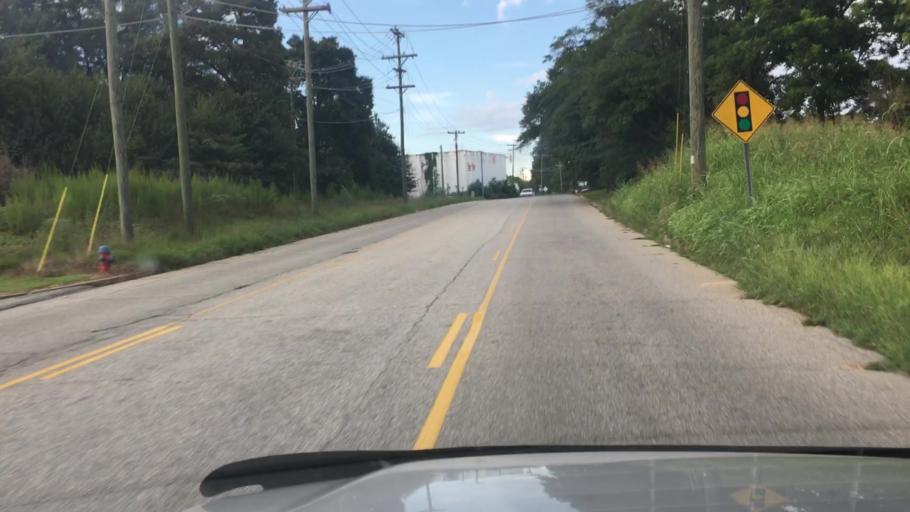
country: US
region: South Carolina
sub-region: Spartanburg County
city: Spartanburg
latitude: 34.9704
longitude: -81.9285
